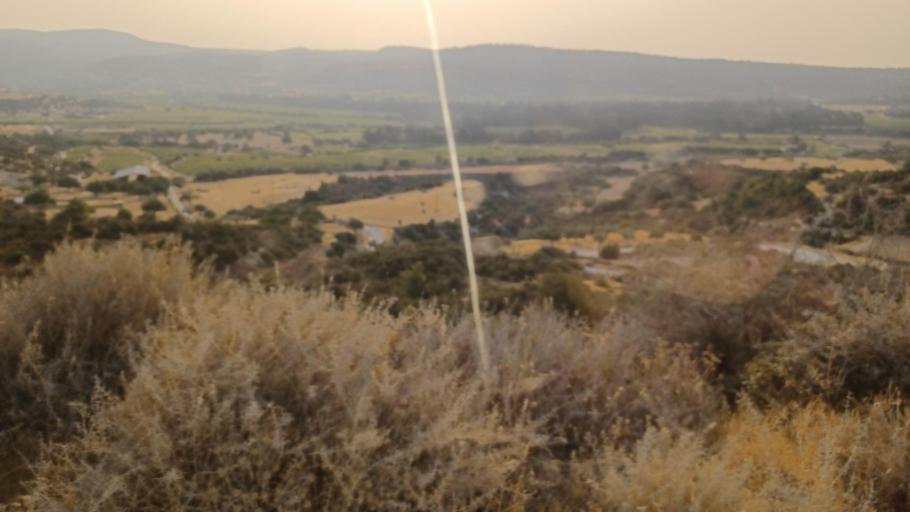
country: CY
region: Limassol
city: Pissouri
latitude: 34.6982
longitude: 32.6607
